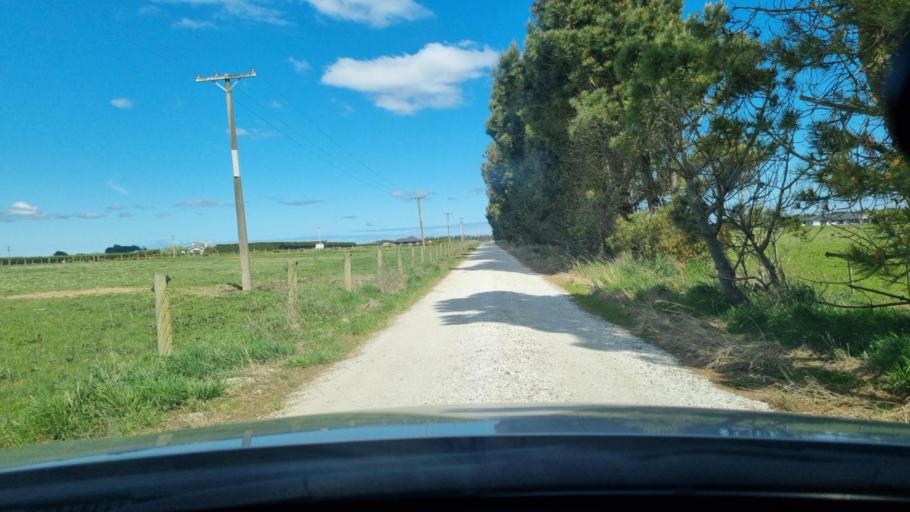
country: NZ
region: Southland
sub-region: Invercargill City
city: Invercargill
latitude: -46.3668
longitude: 168.2828
